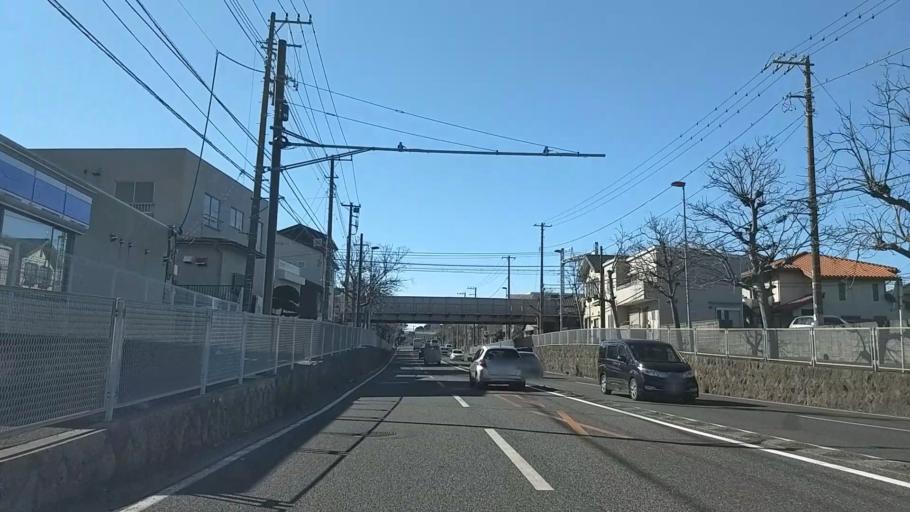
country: JP
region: Kanagawa
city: Yokosuka
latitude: 35.2628
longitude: 139.6930
